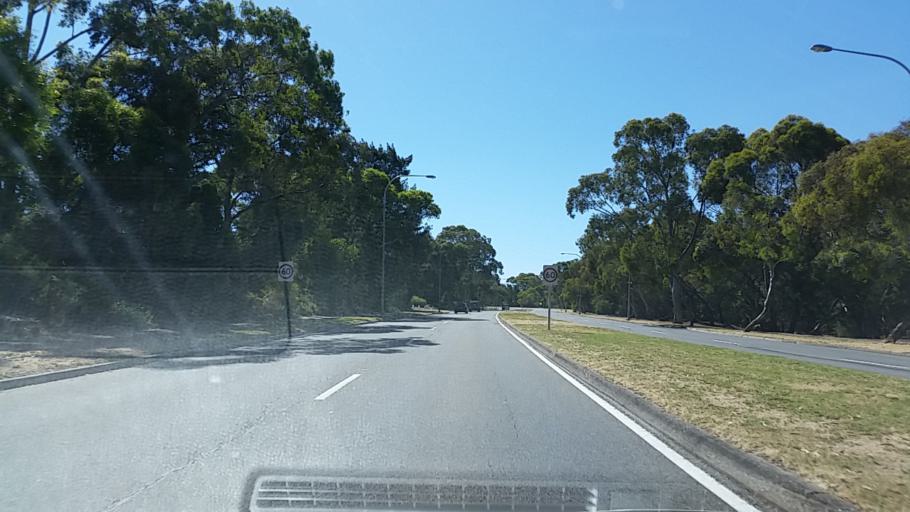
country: AU
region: South Australia
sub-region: Tea Tree Gully
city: Hope Valley
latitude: -34.8059
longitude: 138.6927
